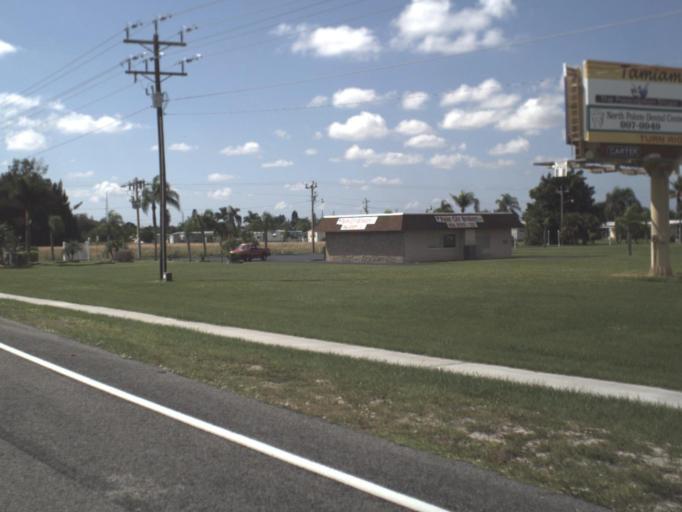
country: US
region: Florida
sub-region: Lee County
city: Palmona Park
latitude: 26.7033
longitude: -81.9002
